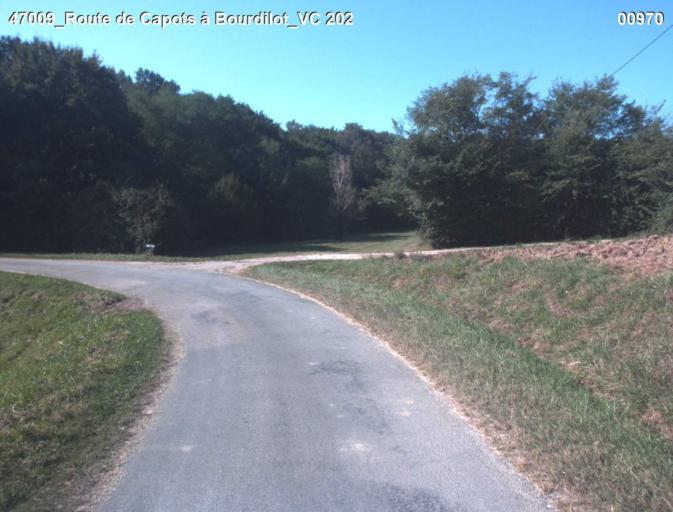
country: FR
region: Aquitaine
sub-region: Departement du Lot-et-Garonne
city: Mezin
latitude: 44.1014
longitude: 0.2976
